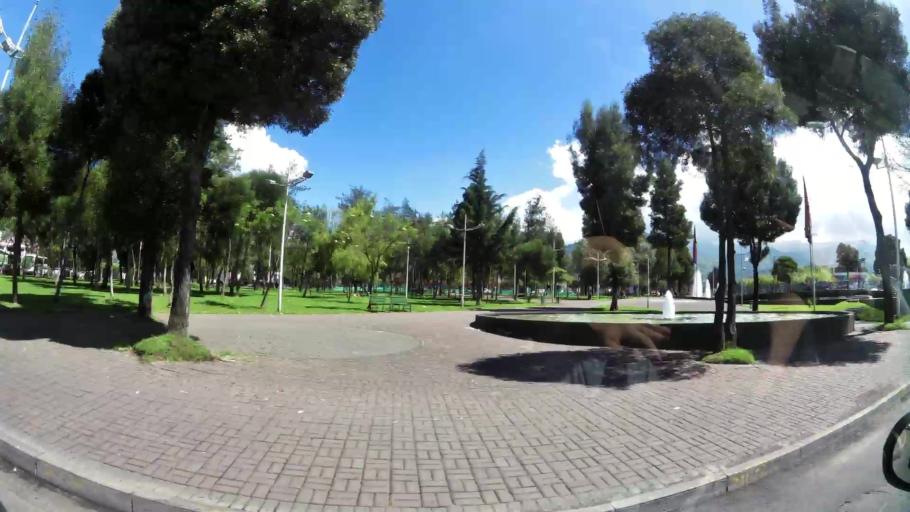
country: EC
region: Pichincha
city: Quito
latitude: -0.2734
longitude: -78.5369
